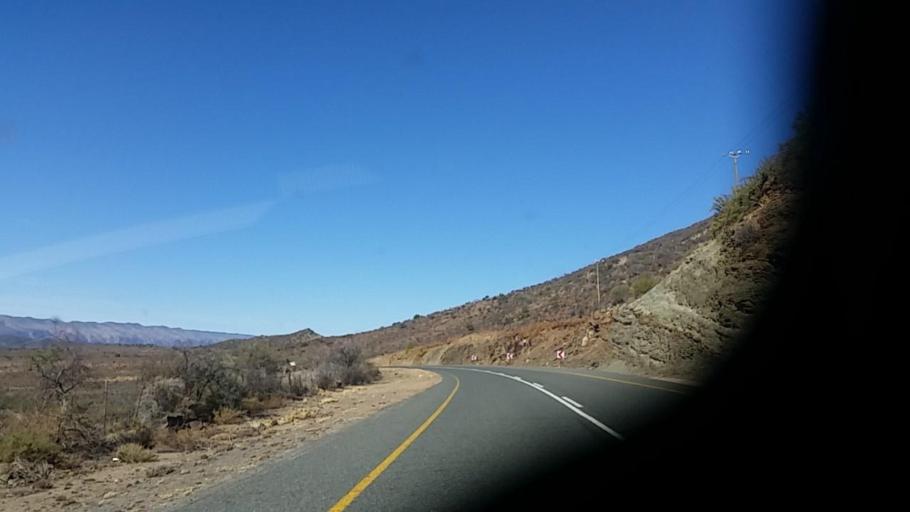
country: ZA
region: Eastern Cape
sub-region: Cacadu District Municipality
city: Willowmore
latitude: -33.4959
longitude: 23.0076
